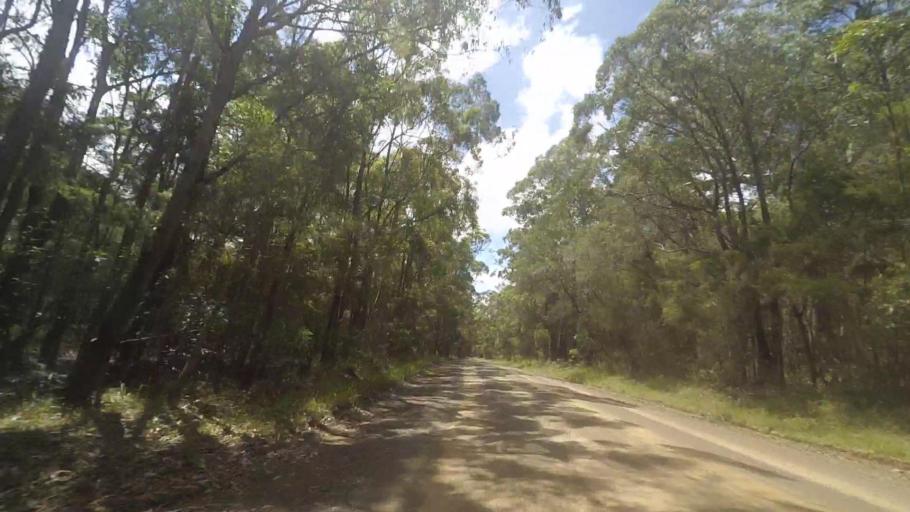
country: AU
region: New South Wales
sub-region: Great Lakes
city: Bulahdelah
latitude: -32.4917
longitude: 152.2758
